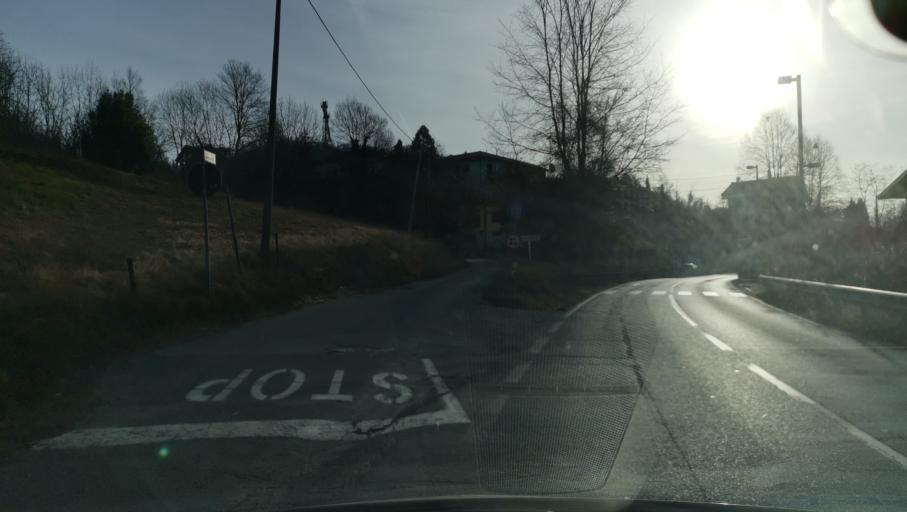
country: IT
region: Piedmont
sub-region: Provincia di Torino
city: Castiglione Torinese
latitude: 45.1056
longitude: 7.8194
